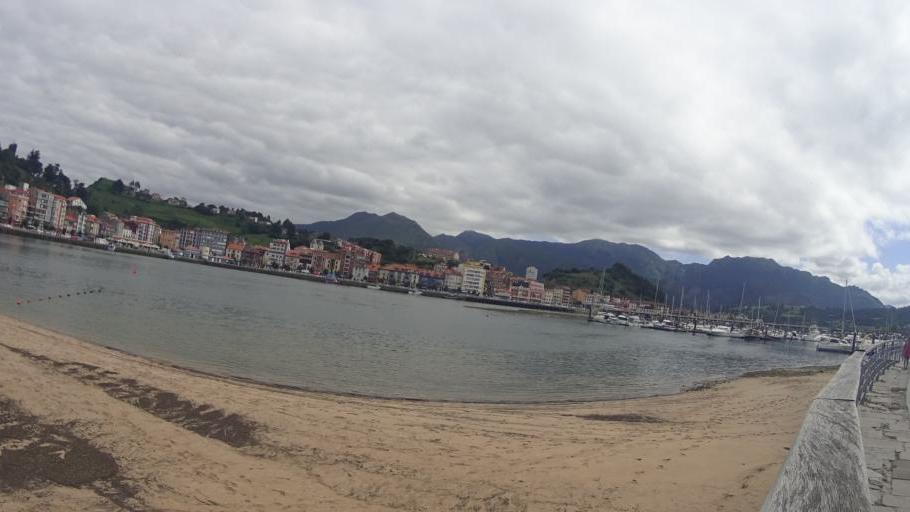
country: ES
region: Asturias
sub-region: Province of Asturias
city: Ribadesella
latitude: 43.4656
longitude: -5.0624
